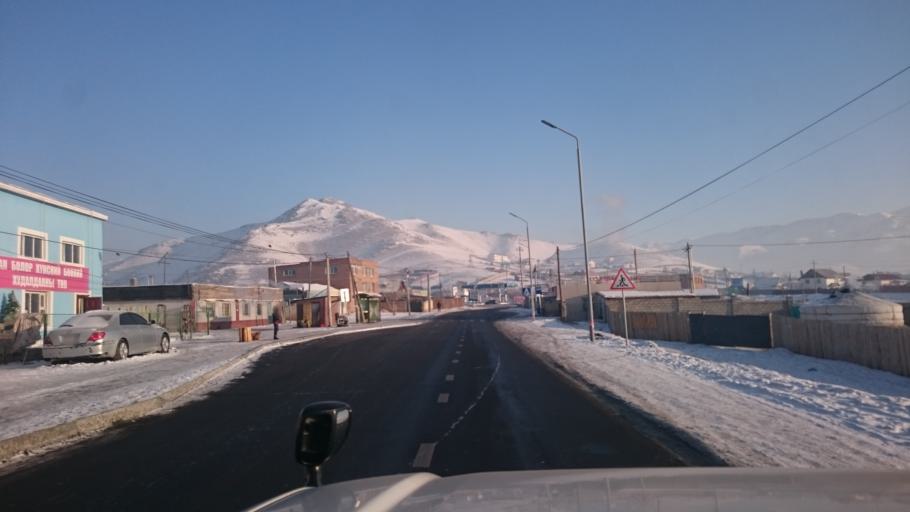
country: MN
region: Ulaanbaatar
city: Ulaanbaatar
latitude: 47.9268
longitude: 107.1431
